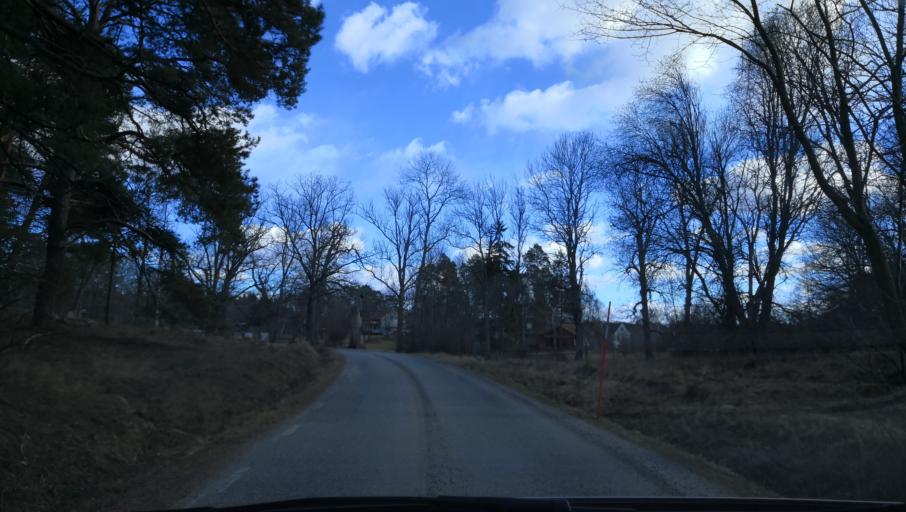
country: SE
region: Stockholm
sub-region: Varmdo Kommun
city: Mortnas
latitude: 59.3803
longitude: 18.4579
